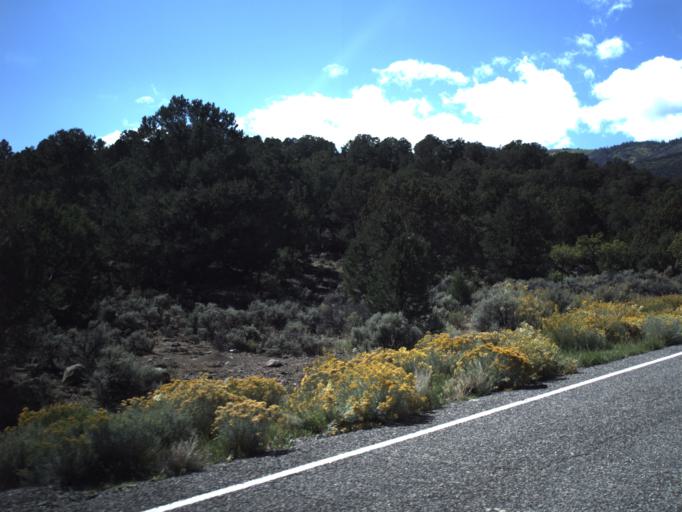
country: US
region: Utah
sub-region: Piute County
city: Junction
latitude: 38.2569
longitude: -112.2816
